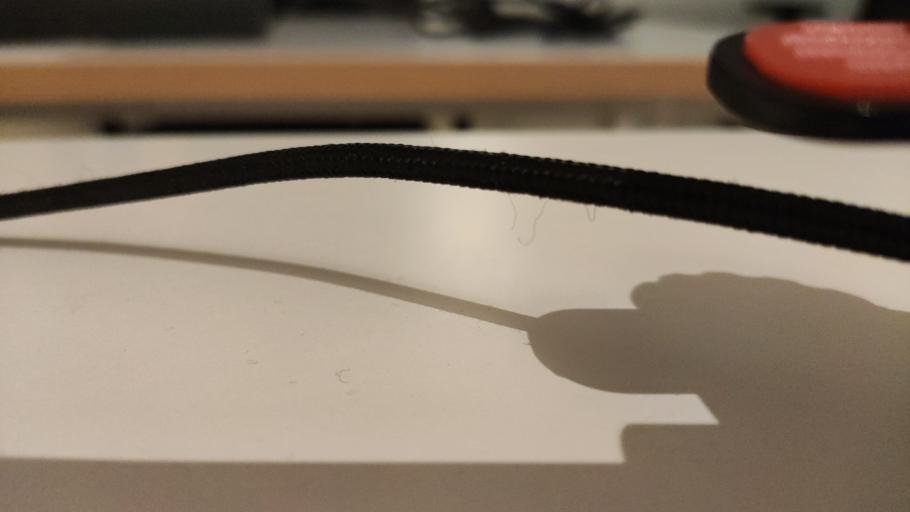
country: RU
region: Moskovskaya
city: Konstantinovo
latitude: 56.4178
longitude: 37.9874
